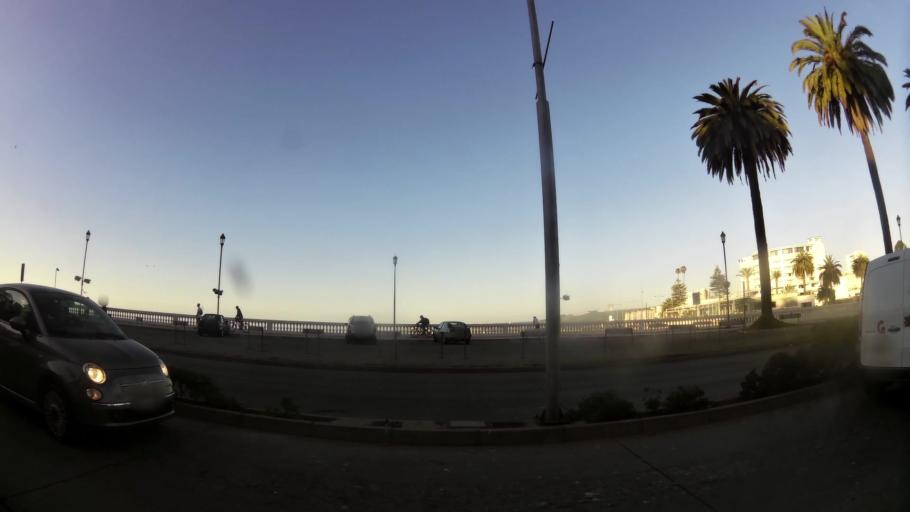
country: CL
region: Valparaiso
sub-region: Provincia de Valparaiso
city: Vina del Mar
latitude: -33.0199
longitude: -71.5627
